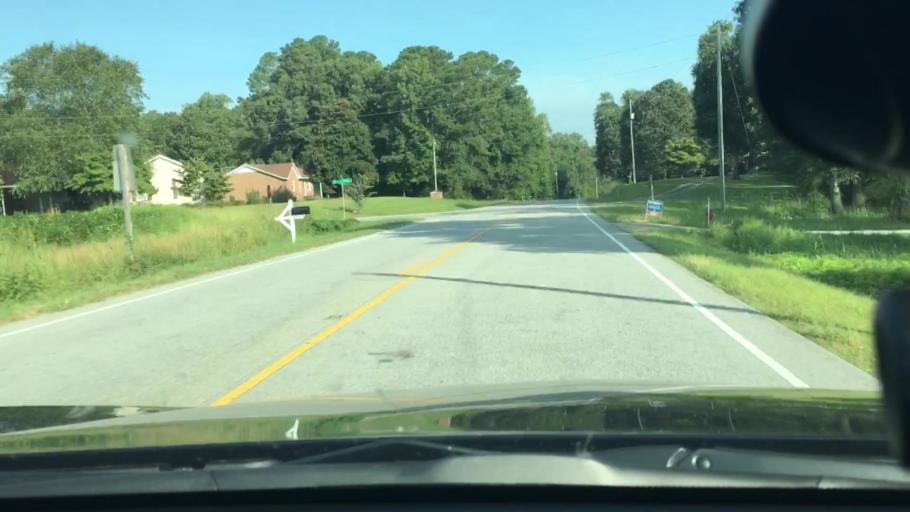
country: US
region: North Carolina
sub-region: Edgecombe County
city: Pinetops
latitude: 35.7182
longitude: -77.5276
